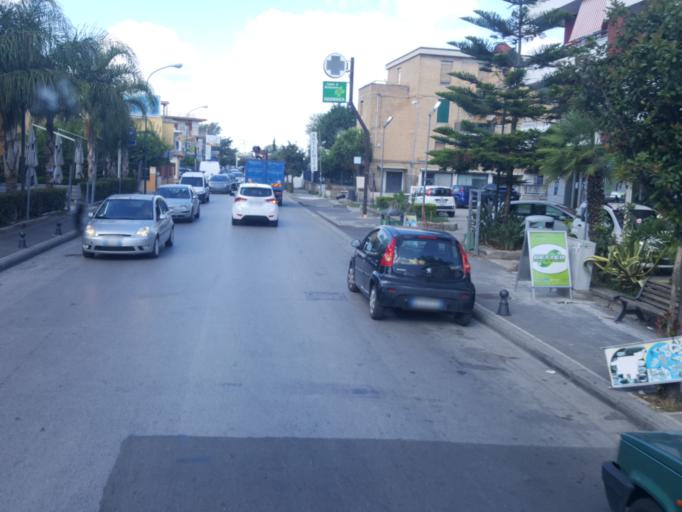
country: IT
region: Campania
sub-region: Provincia di Napoli
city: Nola
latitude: 40.9169
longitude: 14.5231
